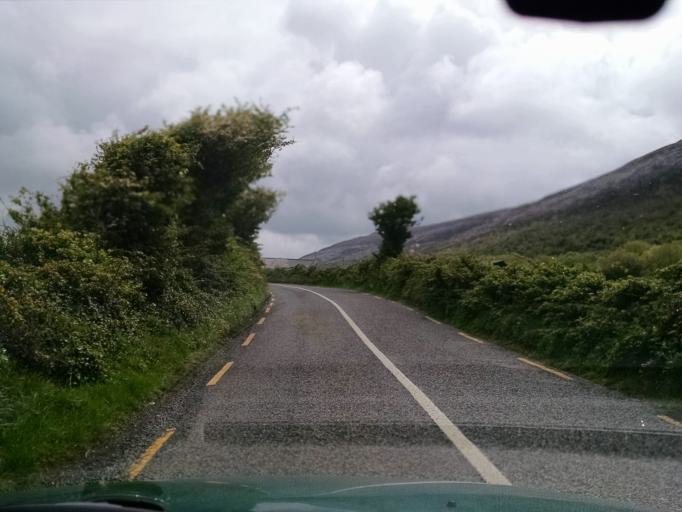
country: IE
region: Connaught
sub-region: County Galway
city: Bearna
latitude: 53.1410
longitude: -9.2283
